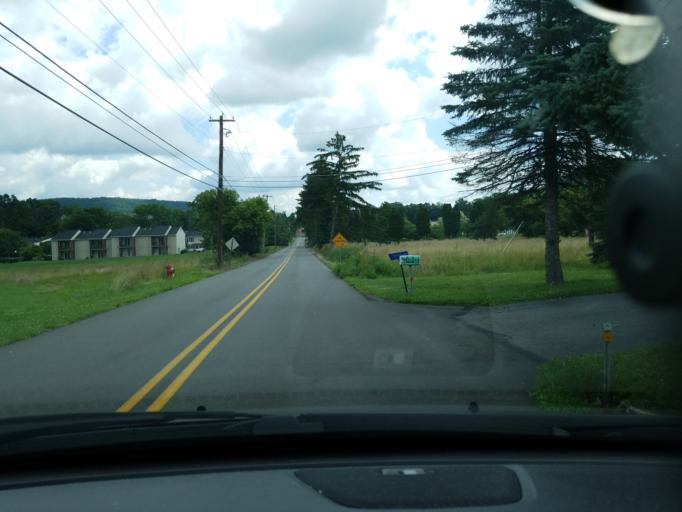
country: US
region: Pennsylvania
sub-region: Northumberland County
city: Elysburg
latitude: 40.8587
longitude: -76.5443
